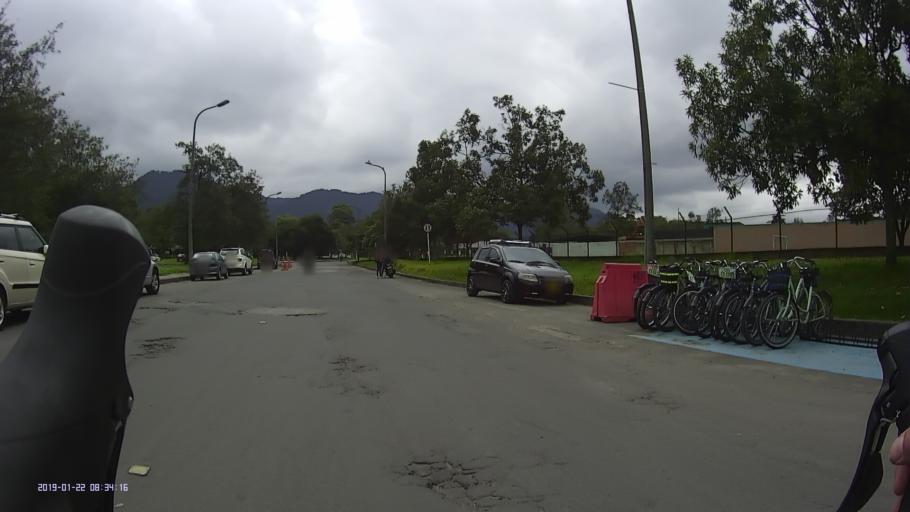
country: CO
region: Bogota D.C.
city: Bogota
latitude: 4.6427
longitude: -74.0834
